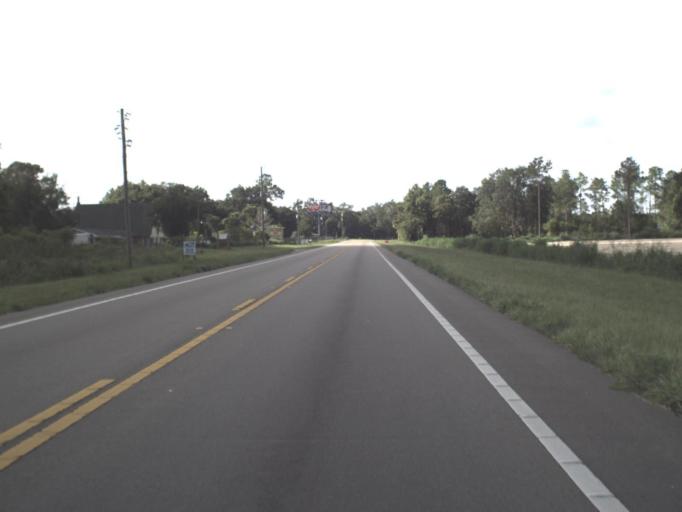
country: US
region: Florida
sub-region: Pasco County
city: Shady Hills
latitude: 28.3426
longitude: -82.5022
